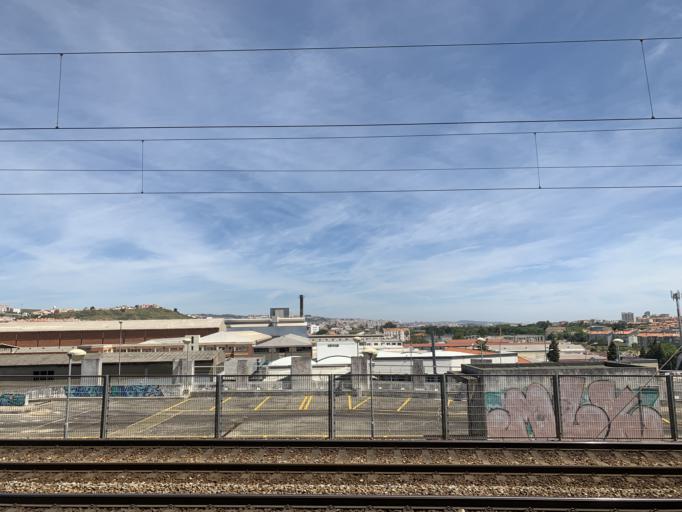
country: PT
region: Lisbon
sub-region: Amadora
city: Amadora
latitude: 38.7504
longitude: -9.2209
